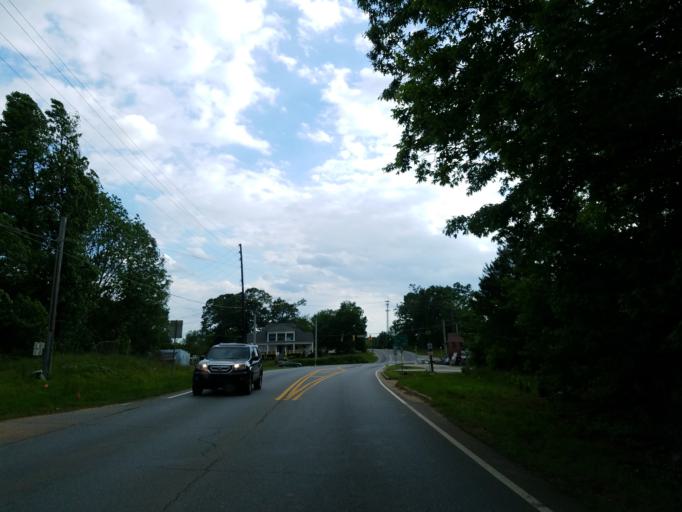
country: US
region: Georgia
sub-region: Fulton County
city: Milton
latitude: 34.2395
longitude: -84.2879
